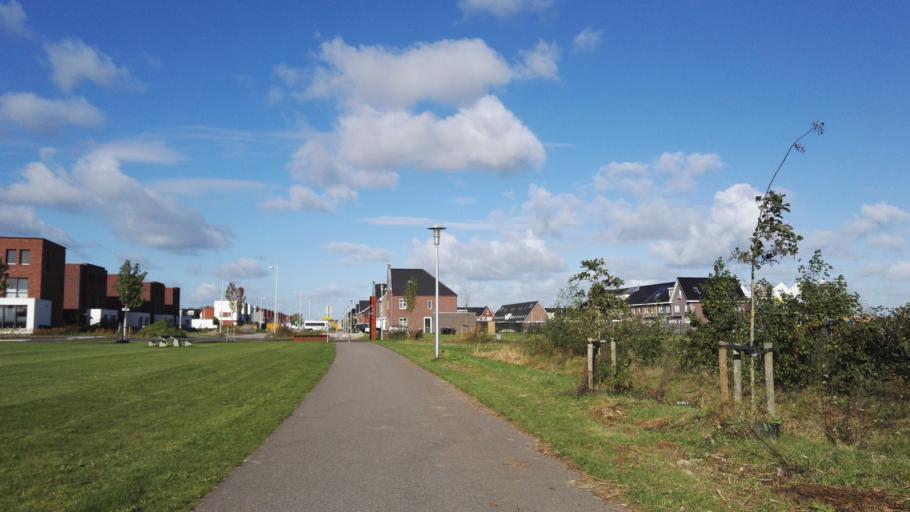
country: NL
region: Gelderland
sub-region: Gemeente Apeldoorn
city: Apeldoorn
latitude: 52.2352
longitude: 6.0032
